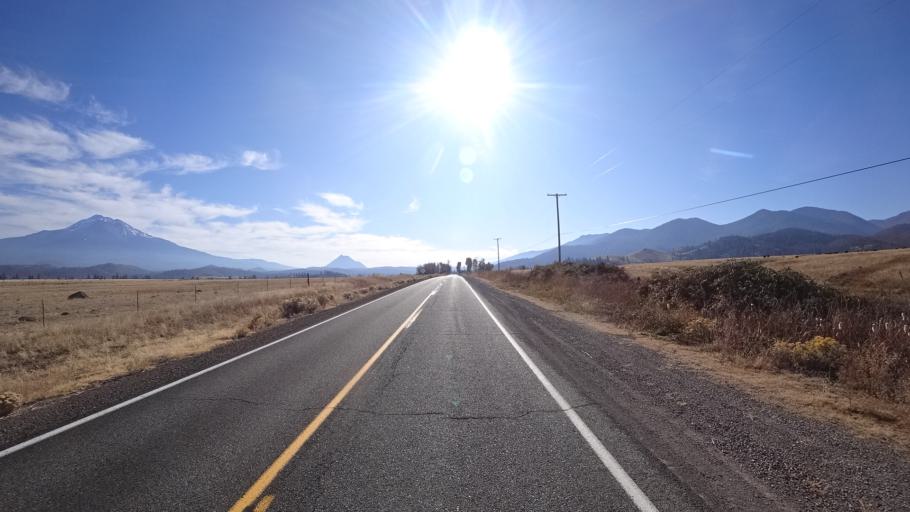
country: US
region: California
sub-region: Siskiyou County
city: Weed
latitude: 41.4638
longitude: -122.4649
